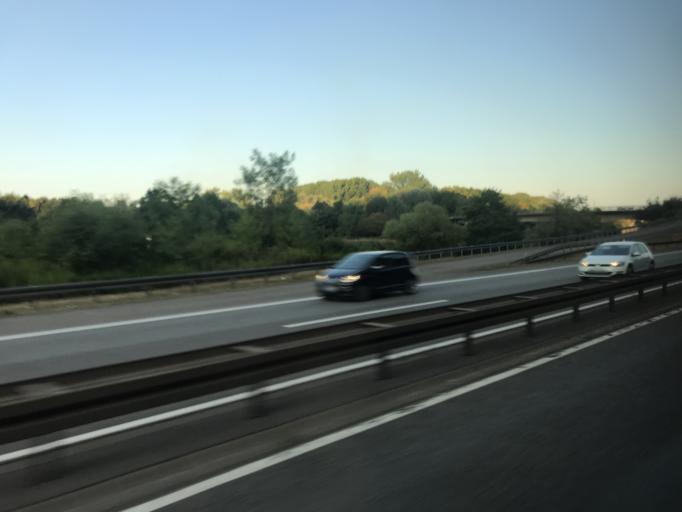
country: DE
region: Saarland
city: Wallerfangen
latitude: 49.3398
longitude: 6.7125
